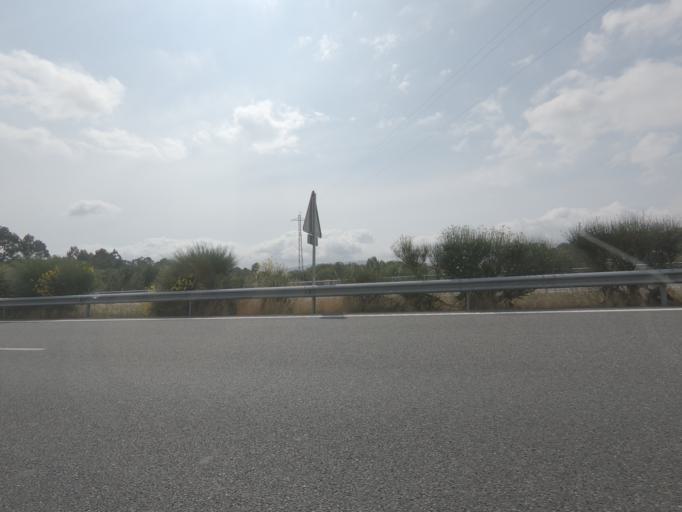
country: ES
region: Galicia
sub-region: Provincia de Ourense
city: Melon
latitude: 42.2098
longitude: -8.2645
